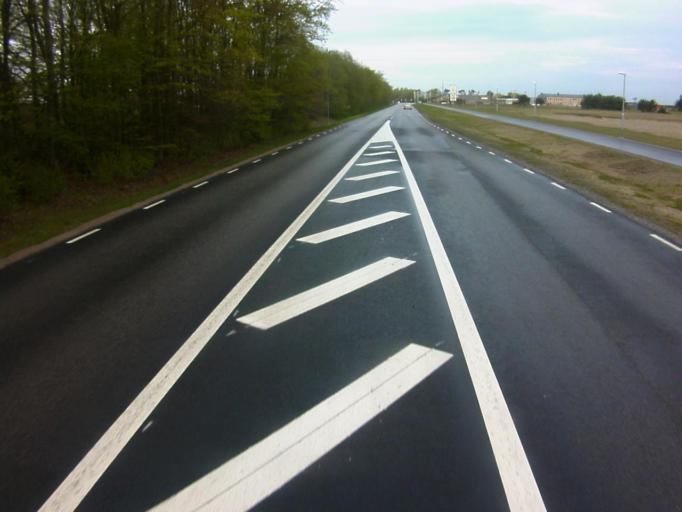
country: SE
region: Skane
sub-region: Kavlinge Kommun
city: Loddekopinge
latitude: 55.7662
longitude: 13.0060
